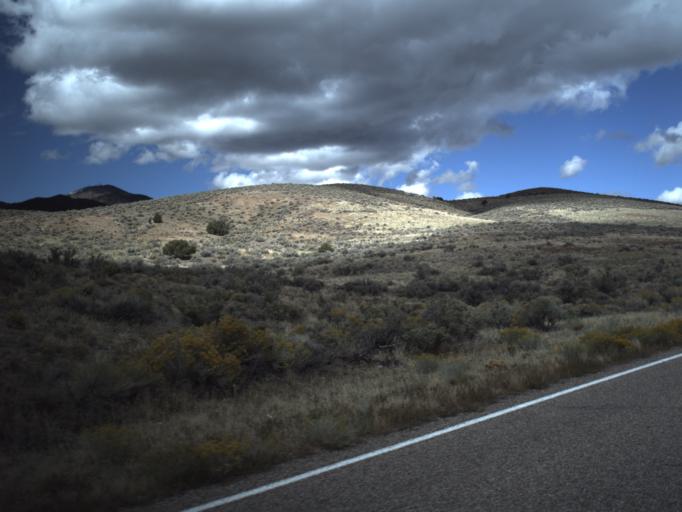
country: US
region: Utah
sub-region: Beaver County
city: Milford
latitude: 38.4427
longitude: -113.2662
